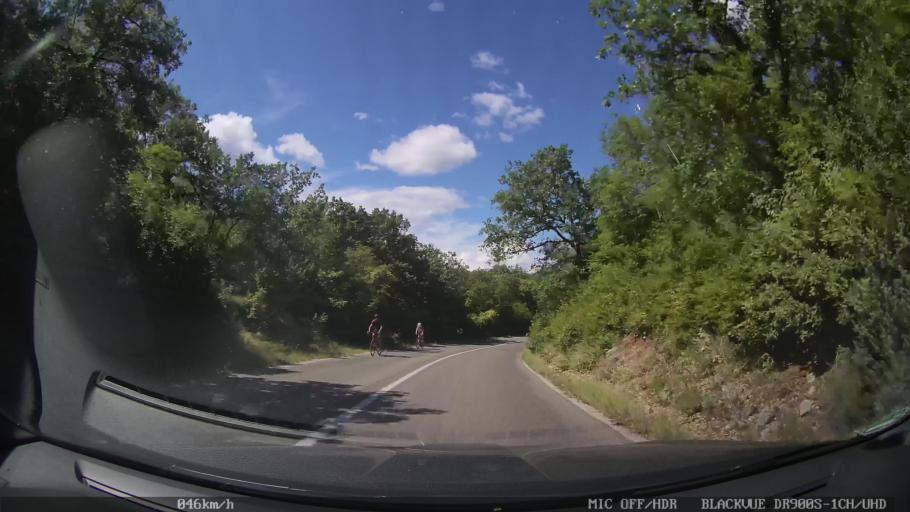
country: HR
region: Primorsko-Goranska
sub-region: Grad Krk
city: Krk
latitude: 45.0459
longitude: 14.5118
